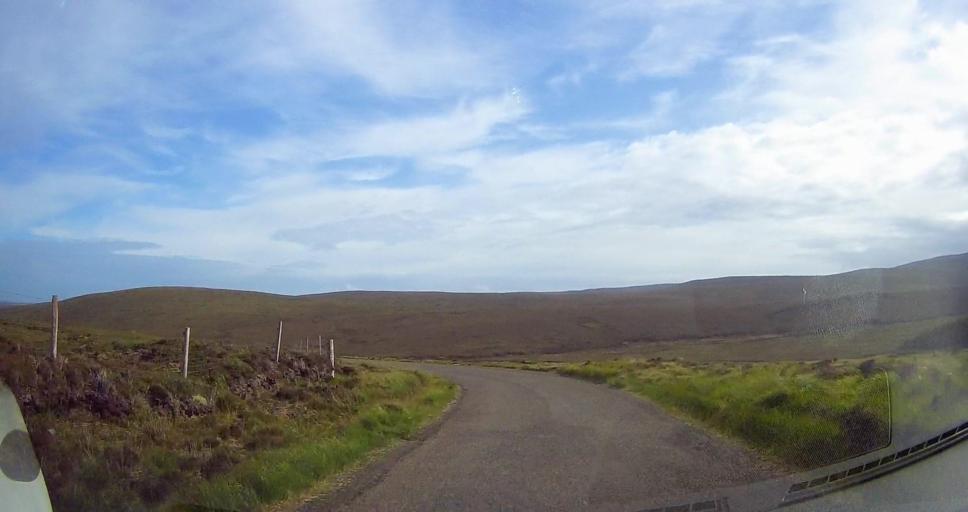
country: GB
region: Scotland
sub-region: Orkney Islands
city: Stromness
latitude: 58.8764
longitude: -3.2469
